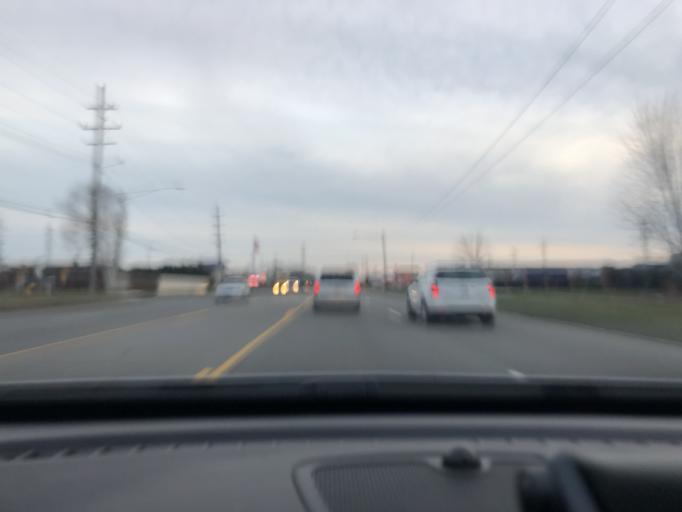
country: US
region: Michigan
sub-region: Wayne County
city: Allen Park
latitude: 42.2440
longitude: -83.2307
